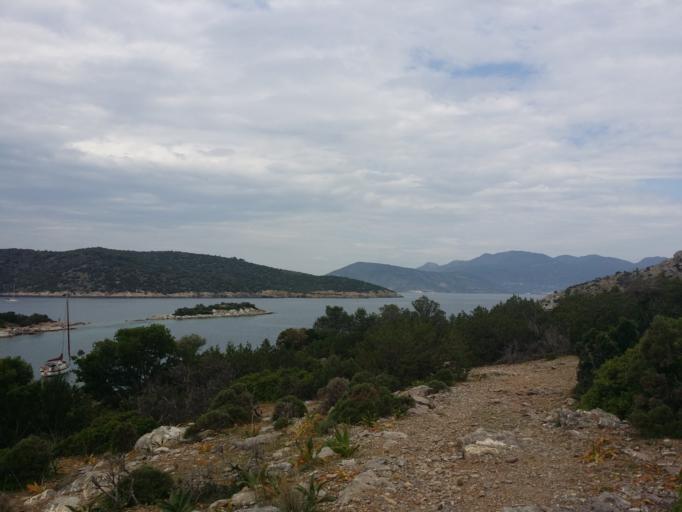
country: GR
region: Attica
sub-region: Nomos Piraios
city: Galatas
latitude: 37.5213
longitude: 23.4281
